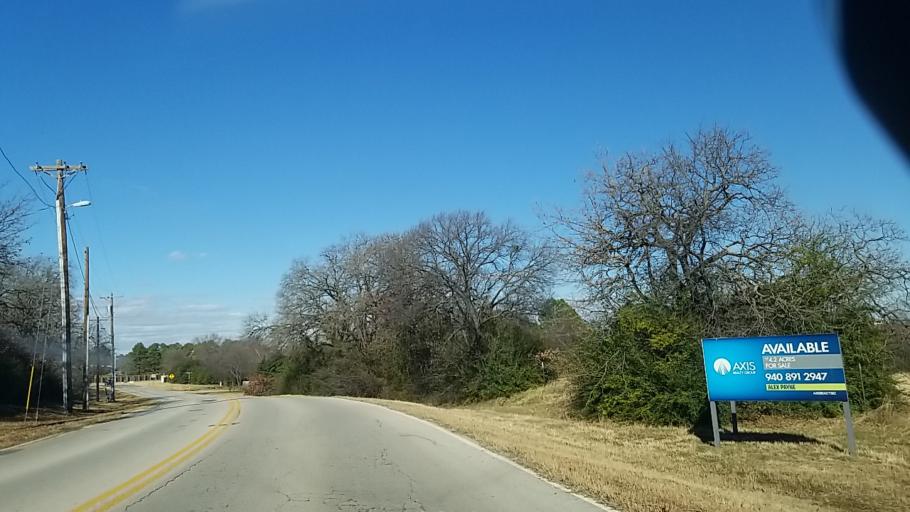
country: US
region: Texas
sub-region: Denton County
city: Corinth
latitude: 33.1631
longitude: -97.0890
